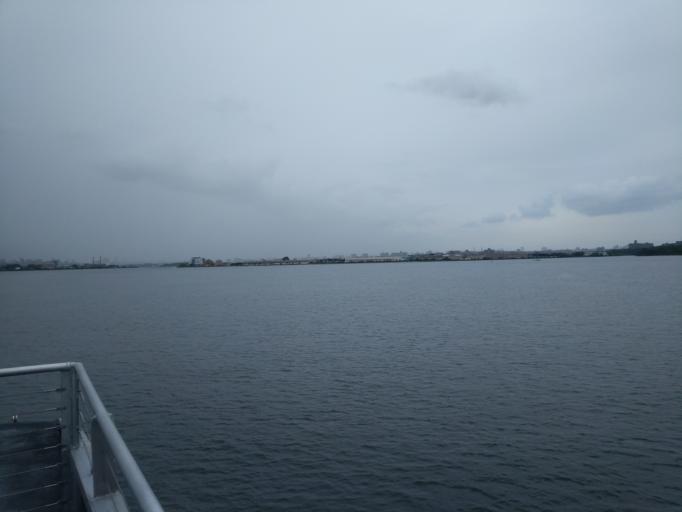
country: US
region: New York
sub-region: Bronx
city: The Bronx
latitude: 40.8015
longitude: -73.8555
